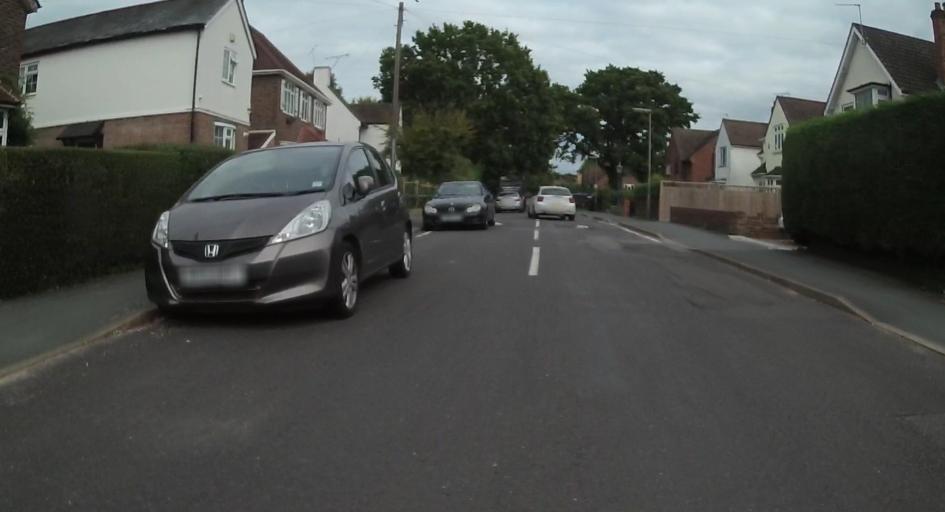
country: GB
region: England
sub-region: Surrey
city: Knaphill
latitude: 51.3172
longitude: -0.6103
